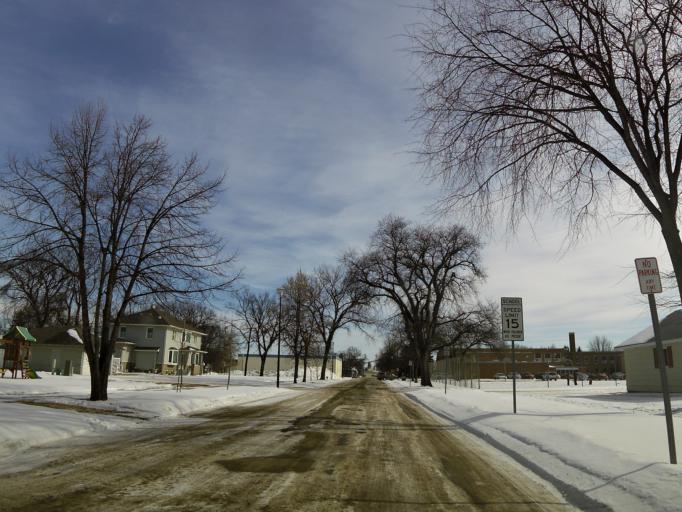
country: US
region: North Dakota
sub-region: Walsh County
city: Grafton
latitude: 48.4175
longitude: -97.4155
